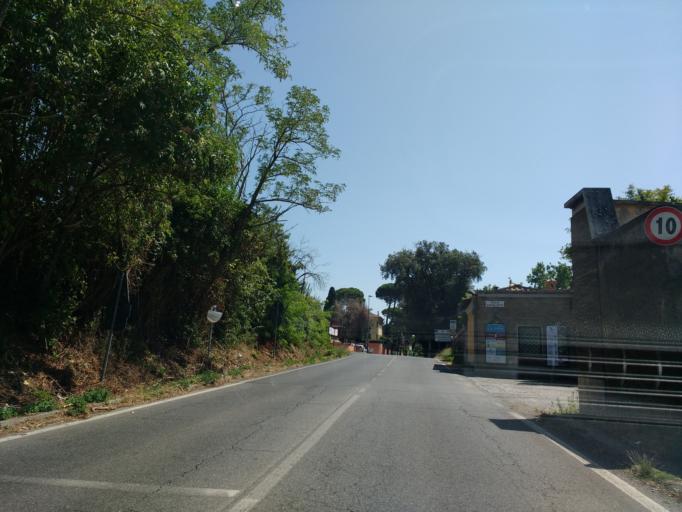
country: IT
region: Latium
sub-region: Citta metropolitana di Roma Capitale
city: Grottaferrata
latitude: 41.7946
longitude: 12.6828
